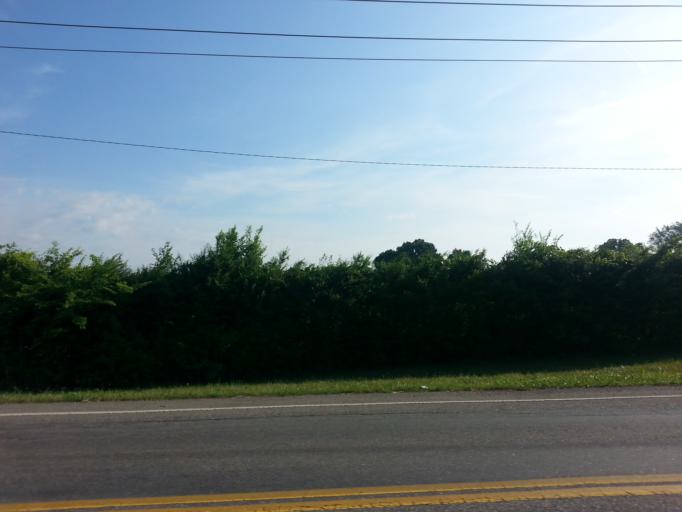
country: US
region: Tennessee
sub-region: Blount County
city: Alcoa
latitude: 35.8044
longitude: -83.9598
